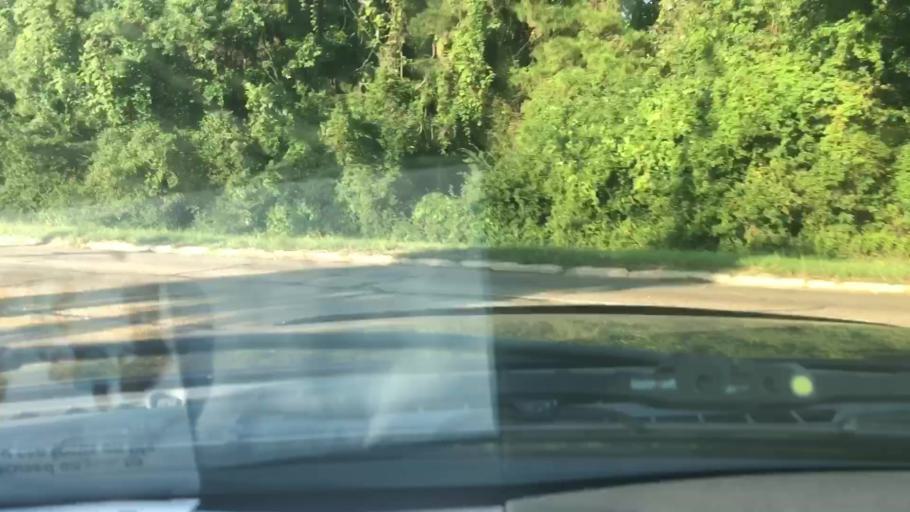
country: US
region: Texas
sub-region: Bowie County
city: Wake Village
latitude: 33.4224
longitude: -94.0802
